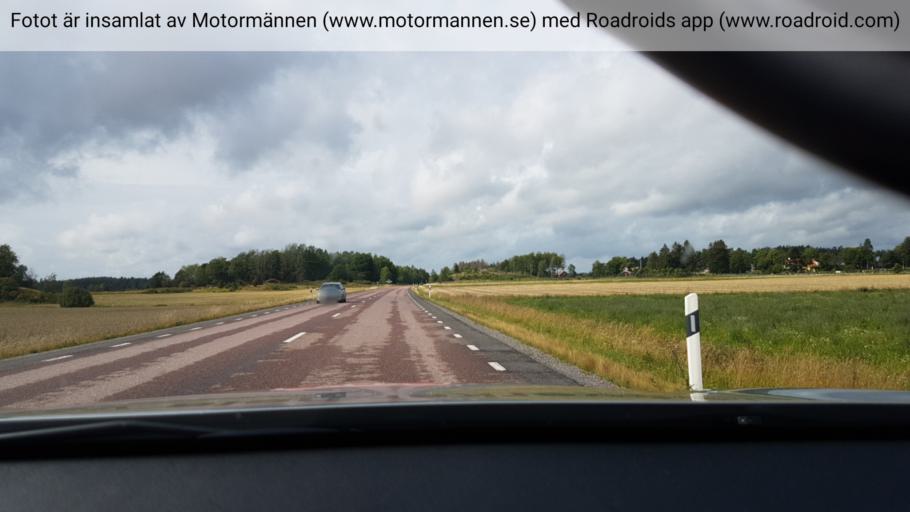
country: SE
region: Uppsala
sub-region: Osthammars Kommun
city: Bjorklinge
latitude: 59.9354
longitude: 17.4641
